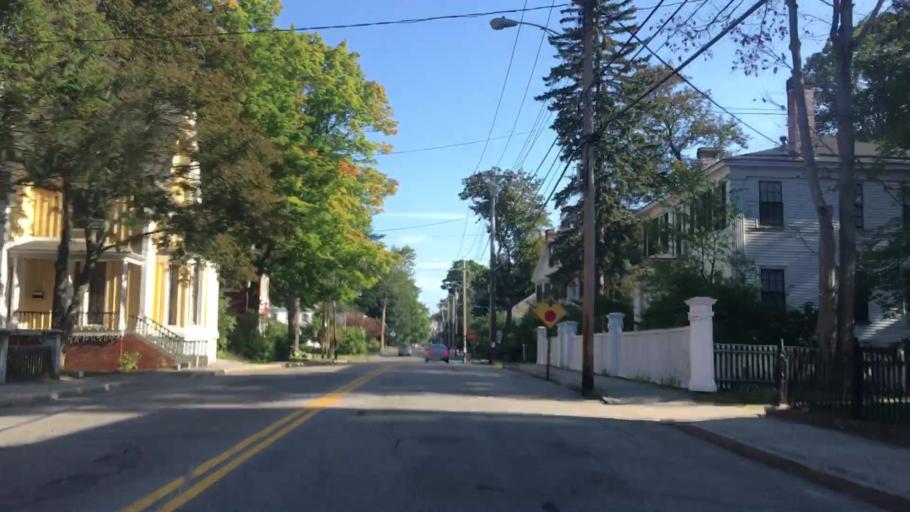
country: US
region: Maine
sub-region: Sagadahoc County
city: Bath
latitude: 43.9181
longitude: -69.8156
